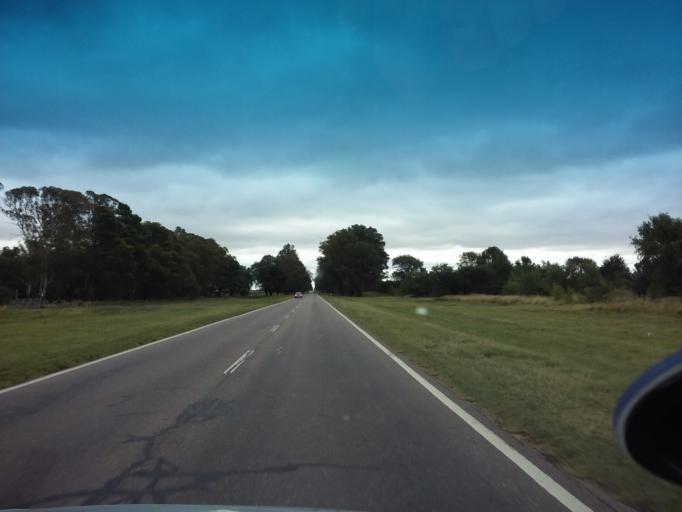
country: AR
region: La Pampa
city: Anguil
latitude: -36.5675
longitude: -64.1346
